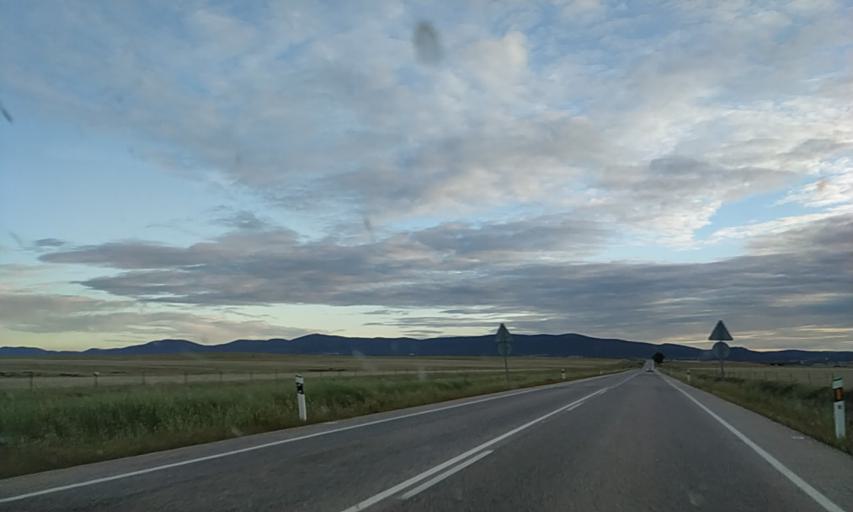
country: ES
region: Extremadura
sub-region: Provincia de Caceres
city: Malpartida de Caceres
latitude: 39.3592
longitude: -6.4643
